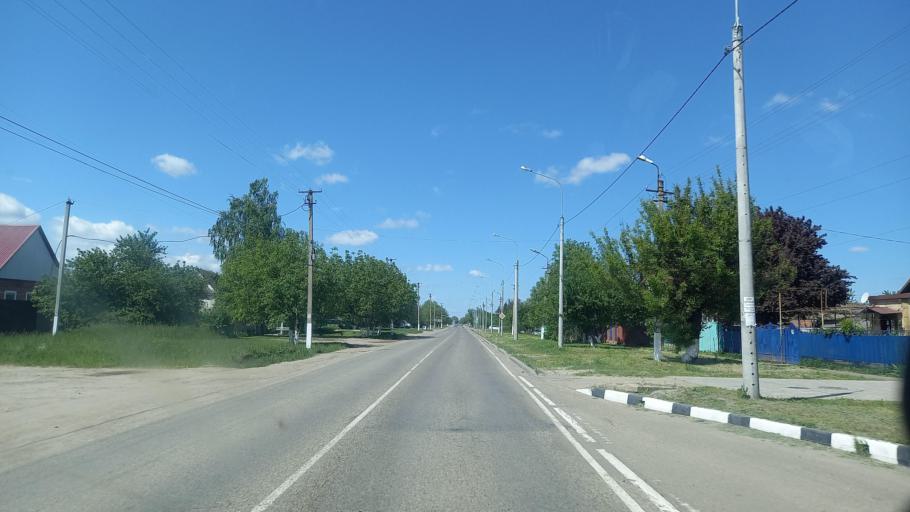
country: RU
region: Krasnodarskiy
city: Novoukrainskoye
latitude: 45.3801
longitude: 40.5348
